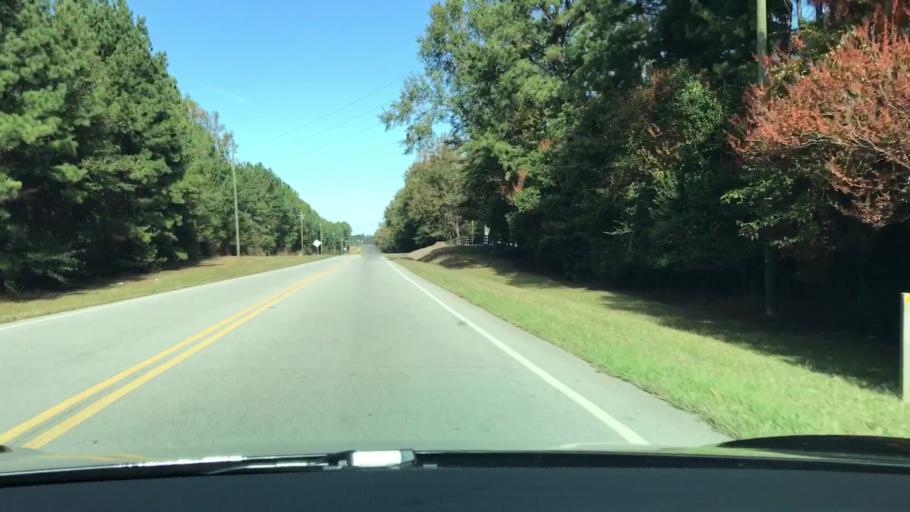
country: US
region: Georgia
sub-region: Warren County
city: Firing Range
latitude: 33.4401
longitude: -82.6914
